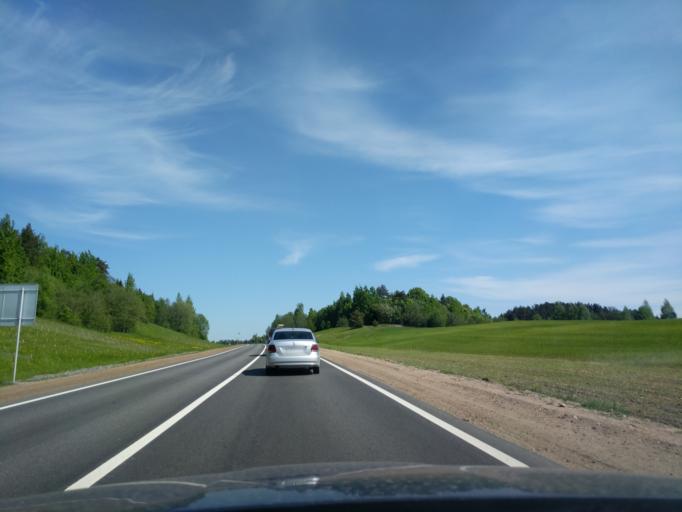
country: BY
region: Minsk
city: Bal'shavik
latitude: 54.0937
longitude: 27.5354
